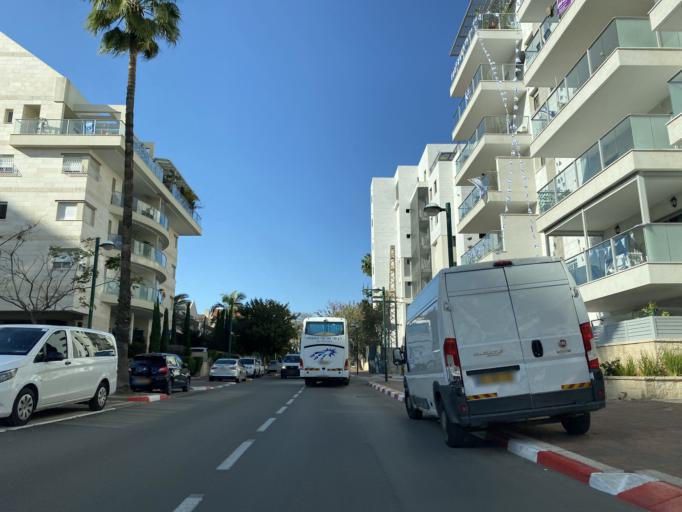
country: IL
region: Central District
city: Kfar Saba
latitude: 32.1777
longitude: 34.9152
